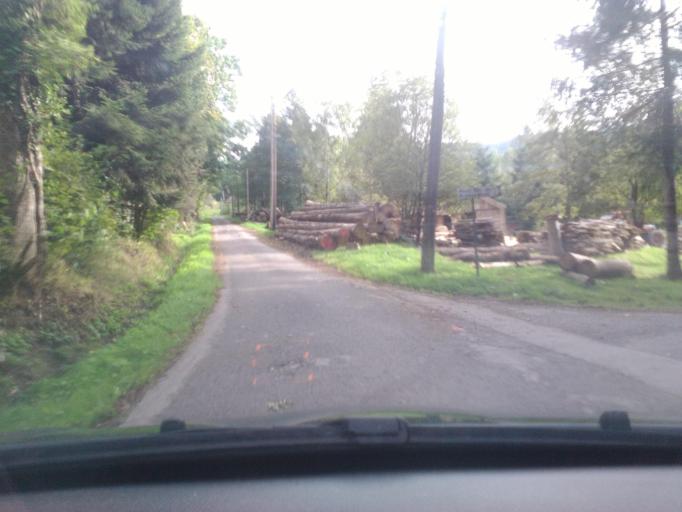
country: FR
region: Lorraine
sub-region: Departement des Vosges
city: Taintrux
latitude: 48.2337
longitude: 6.8635
